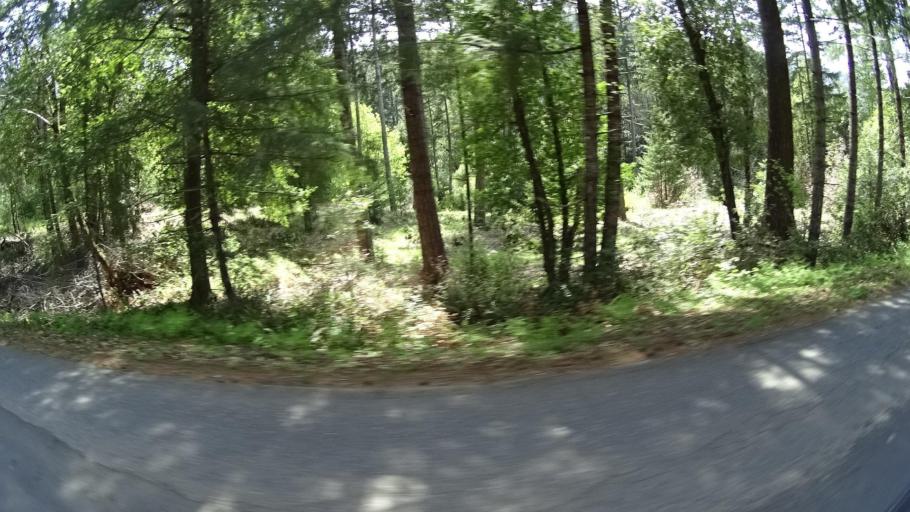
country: US
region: California
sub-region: Humboldt County
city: Redway
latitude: 40.3762
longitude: -123.7415
